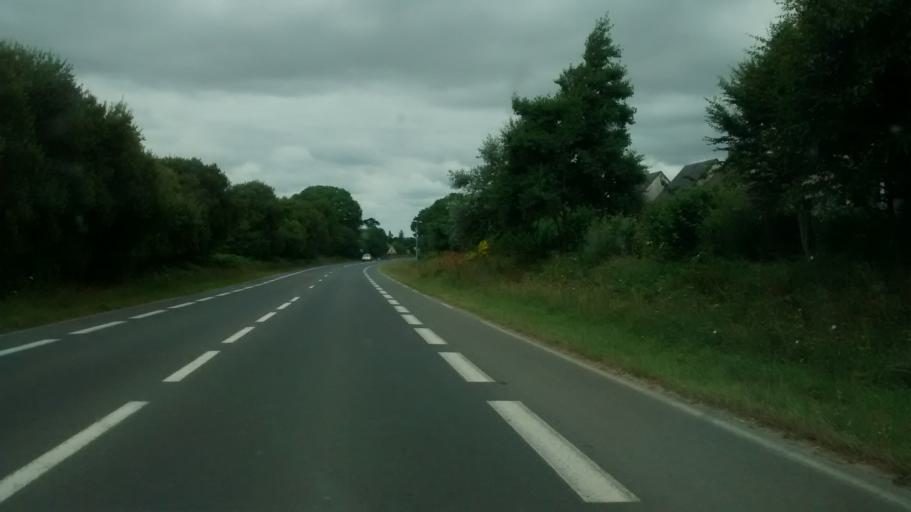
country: FR
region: Brittany
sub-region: Departement du Finistere
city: Plougastel-Daoulas
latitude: 48.3768
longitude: -4.3797
